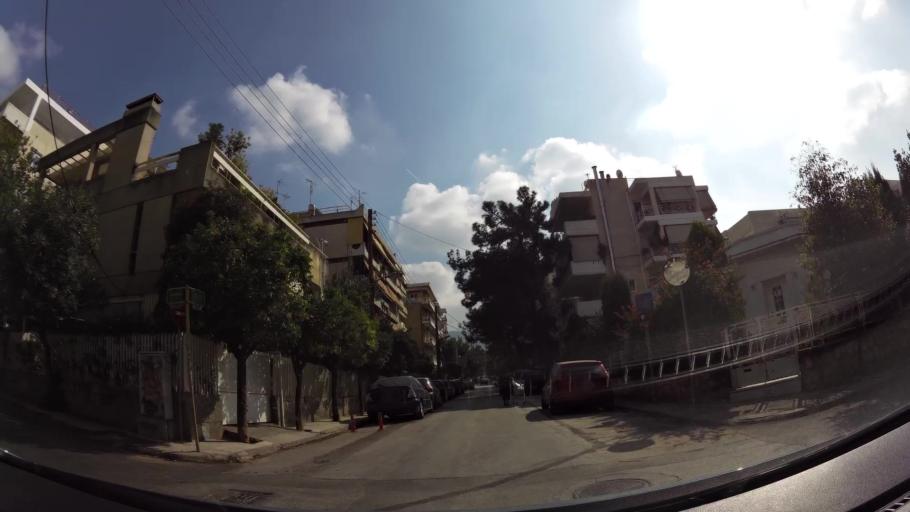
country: GR
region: Attica
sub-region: Nomarchia Athinas
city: Cholargos
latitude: 37.9984
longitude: 23.7944
